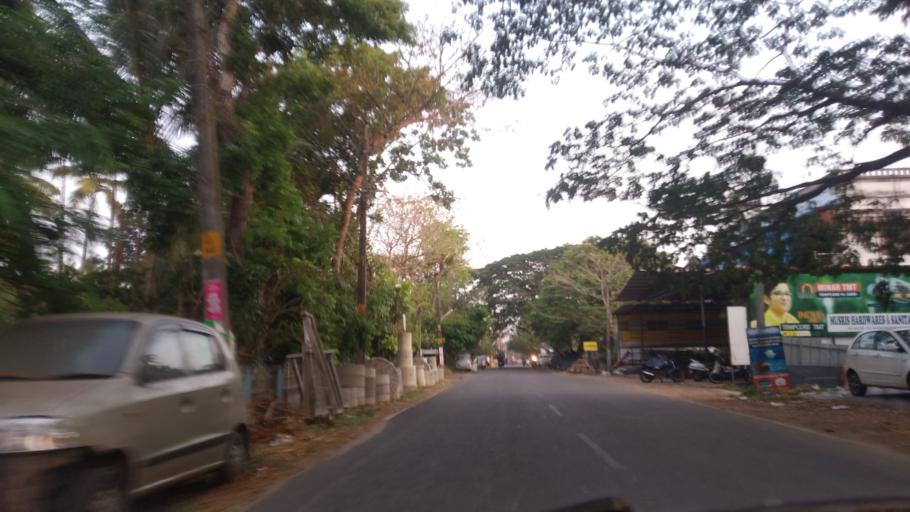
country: IN
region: Kerala
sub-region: Thrissur District
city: Kodungallur
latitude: 10.2133
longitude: 76.1617
